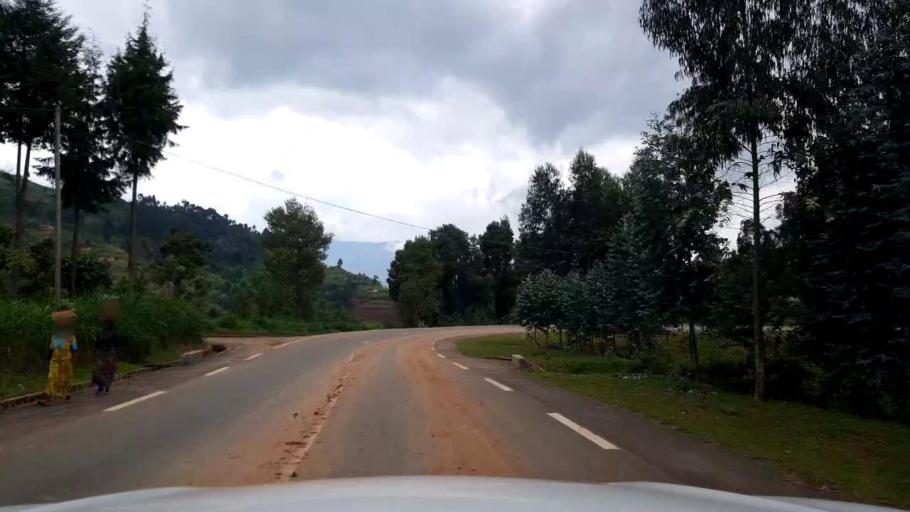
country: RW
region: Western Province
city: Kibuye
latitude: -1.8775
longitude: 29.3510
